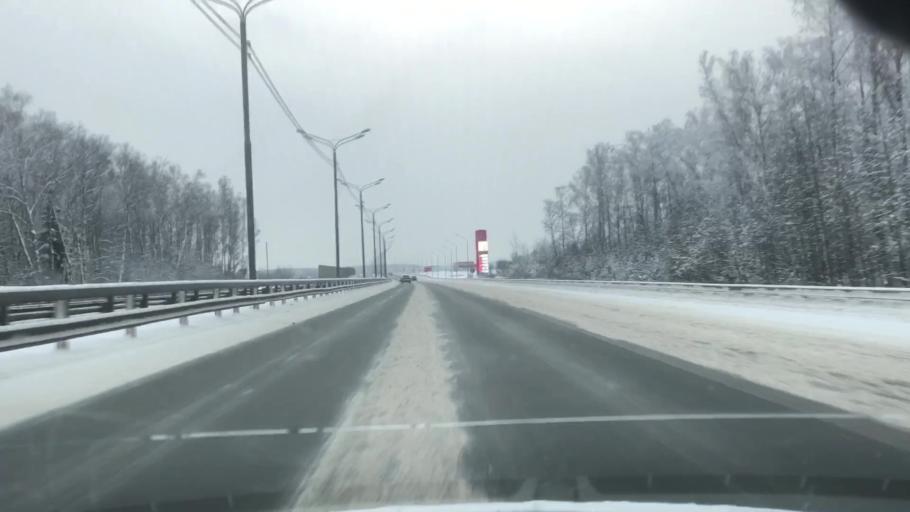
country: RU
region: Moskovskaya
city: Barybino
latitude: 55.1984
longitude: 37.8894
